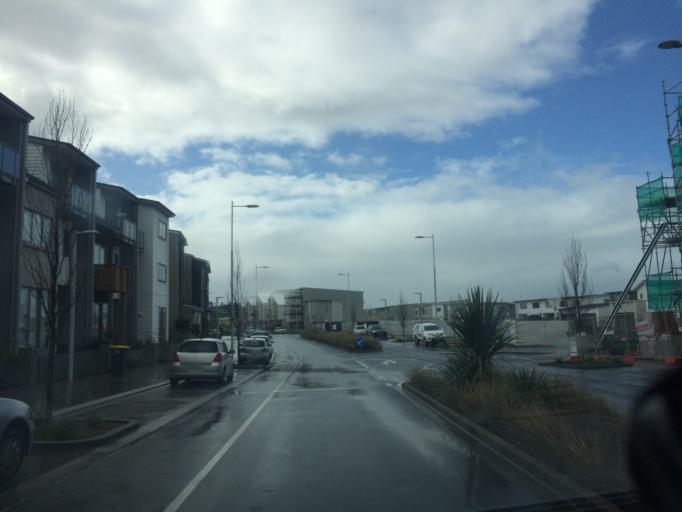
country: NZ
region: Auckland
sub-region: Auckland
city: Rosebank
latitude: -36.7943
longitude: 174.6588
